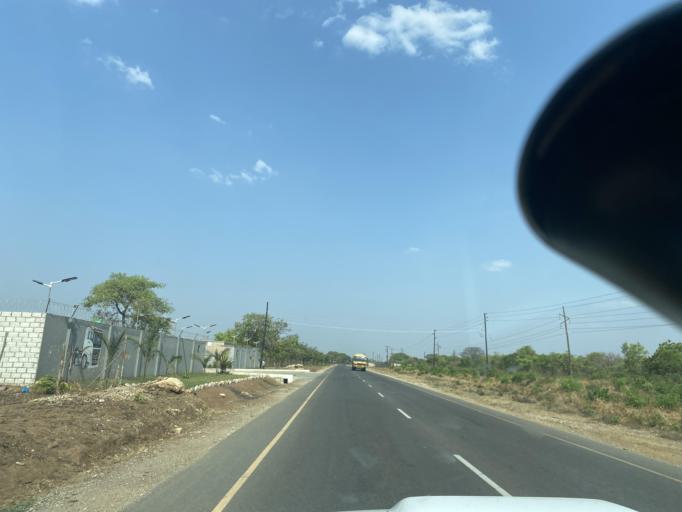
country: ZM
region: Lusaka
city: Lusaka
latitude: -15.3452
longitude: 28.0916
